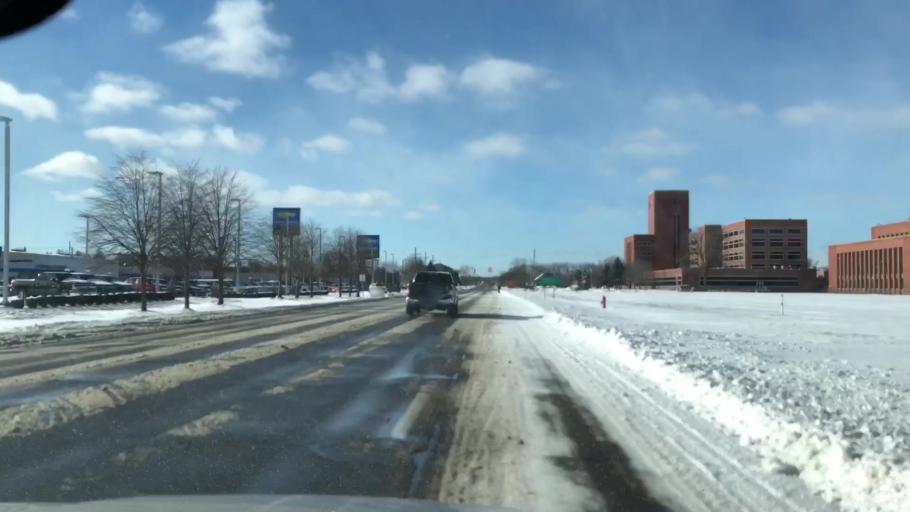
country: US
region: Michigan
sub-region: Wayne County
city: Plymouth
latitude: 42.3742
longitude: -83.4430
